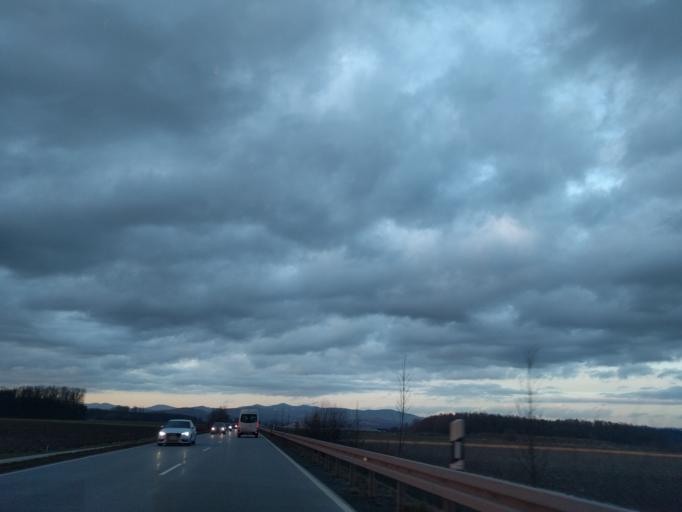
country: DE
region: Bavaria
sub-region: Lower Bavaria
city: Winzer
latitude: 48.7343
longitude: 13.0618
